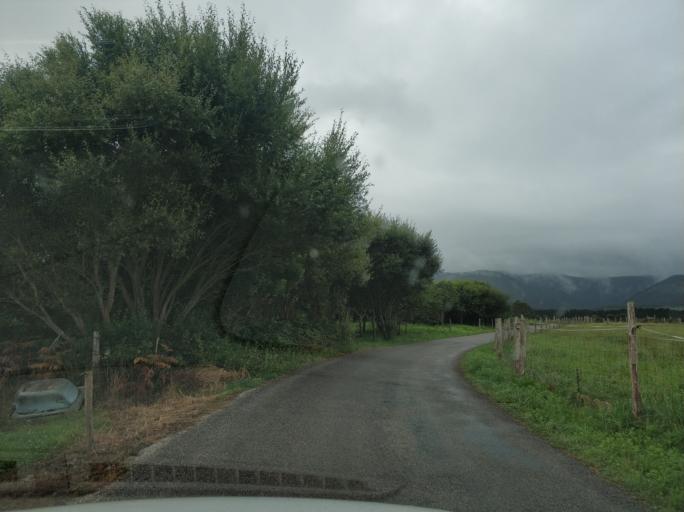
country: ES
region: Asturias
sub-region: Province of Asturias
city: Tineo
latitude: 43.5612
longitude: -6.4679
